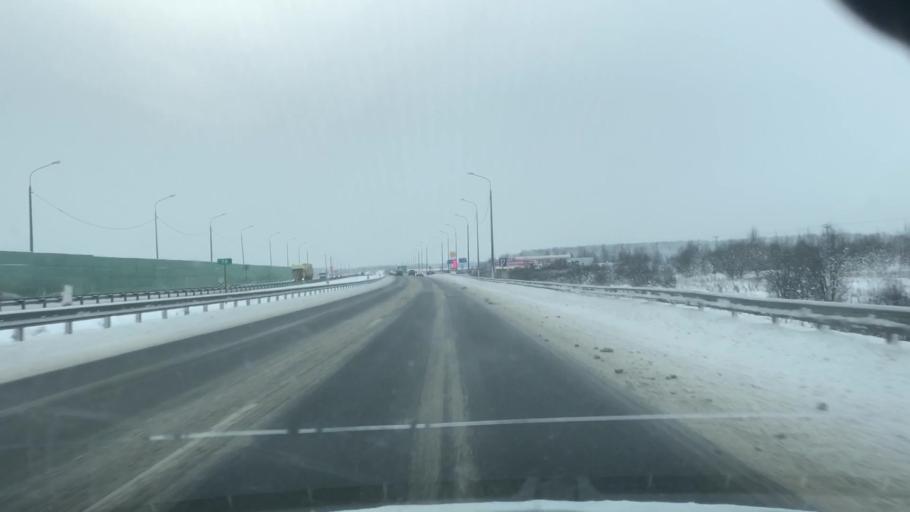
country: RU
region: Moskovskaya
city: Mikhnevo
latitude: 55.0946
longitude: 37.9290
